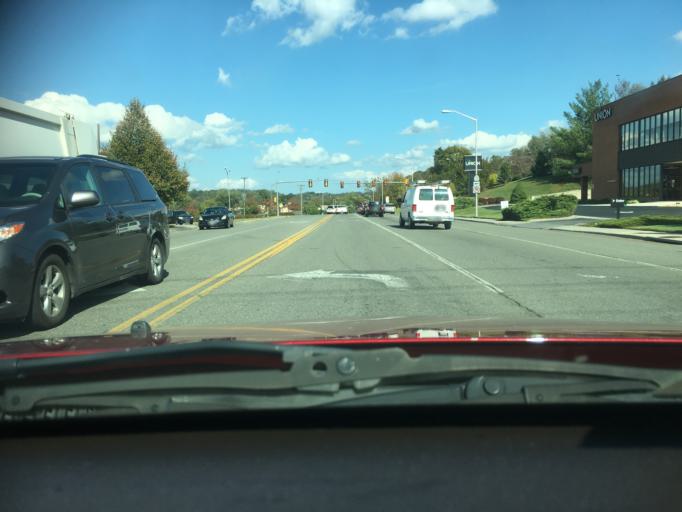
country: US
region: Virginia
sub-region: City of Radford
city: Radford
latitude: 37.1356
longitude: -80.5725
